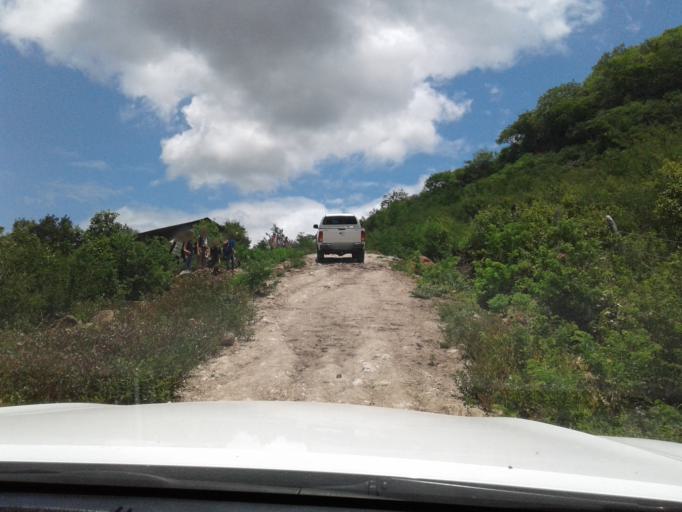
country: NI
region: Matagalpa
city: Ciudad Dario
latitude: 12.6776
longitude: -86.1401
